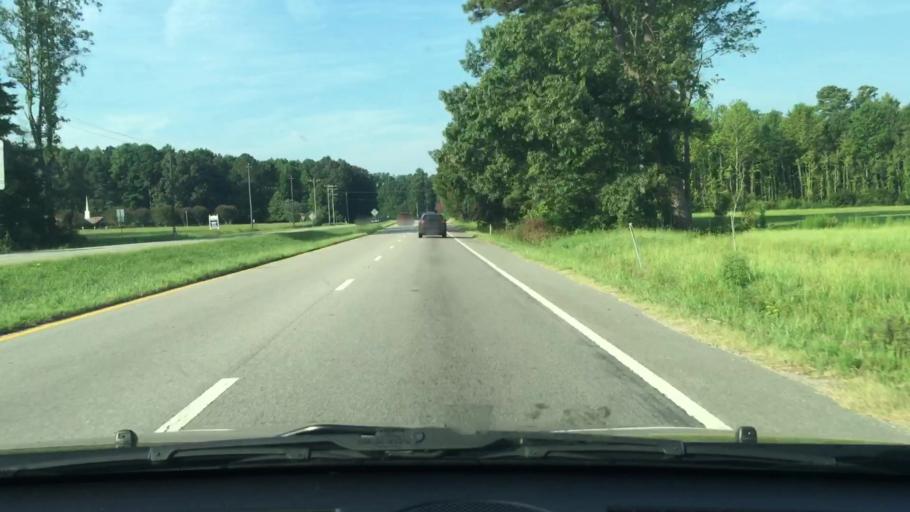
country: US
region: Virginia
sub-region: Isle of Wight County
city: Carrollton
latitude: 36.9508
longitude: -76.5331
